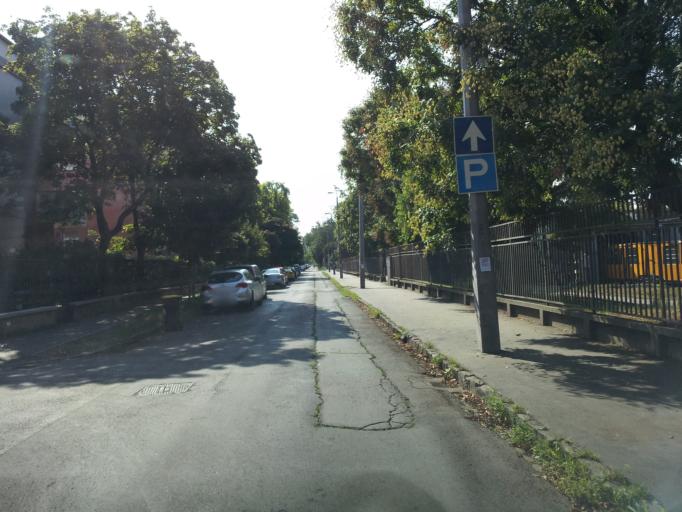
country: HU
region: Budapest
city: Budapest XIV. keruelet
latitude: 47.5189
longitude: 19.0936
